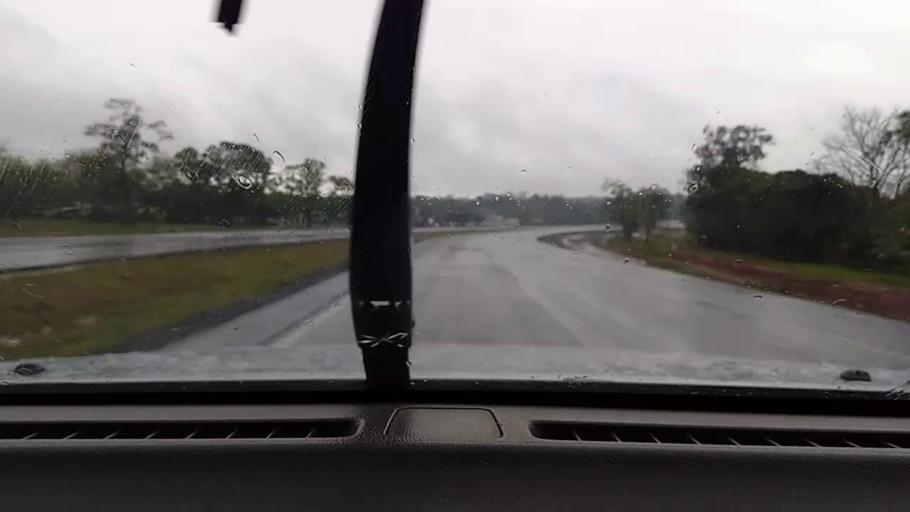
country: PY
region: Caaguazu
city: Repatriacion
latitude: -25.4655
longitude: -55.9329
